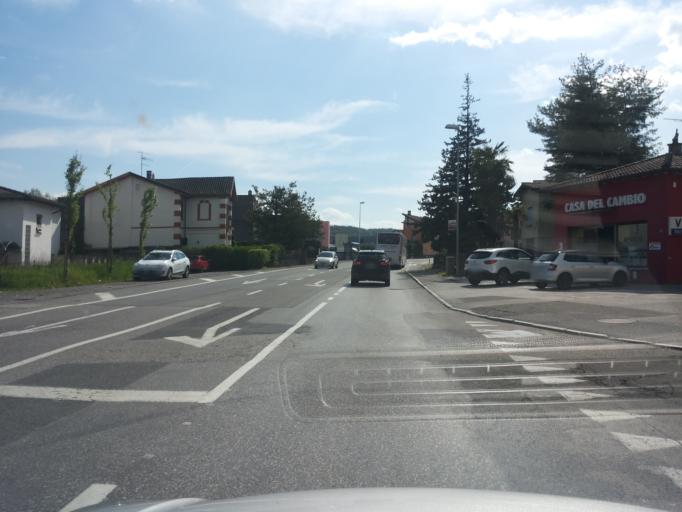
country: CH
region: Ticino
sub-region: Mendrisio District
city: Stabio
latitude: 45.8475
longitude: 8.9354
